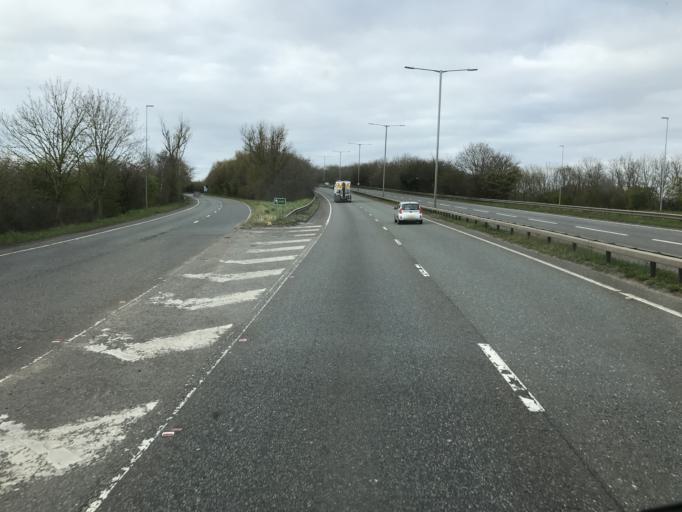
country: GB
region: England
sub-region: Borough of Halton
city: Hale
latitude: 53.3573
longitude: -2.8033
